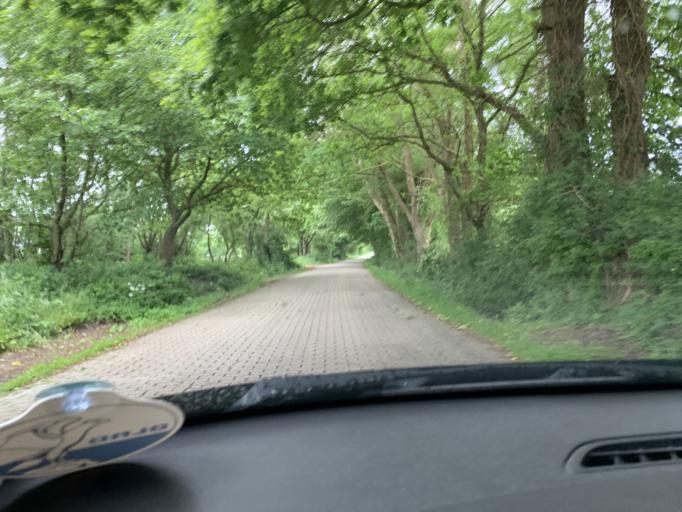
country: DE
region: Lower Saxony
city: Zetel
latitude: 53.4002
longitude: 7.9457
